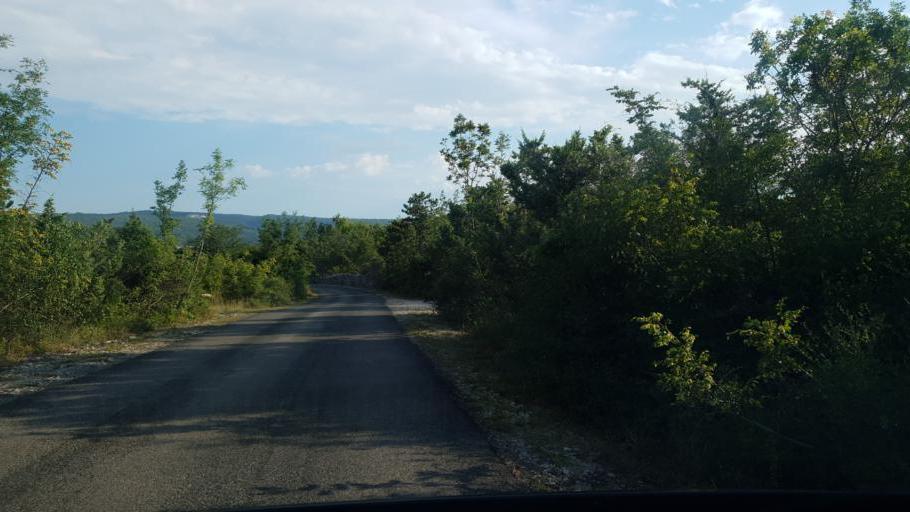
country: HR
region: Primorsko-Goranska
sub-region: Grad Crikvenica
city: Jadranovo
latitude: 45.1744
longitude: 14.6064
